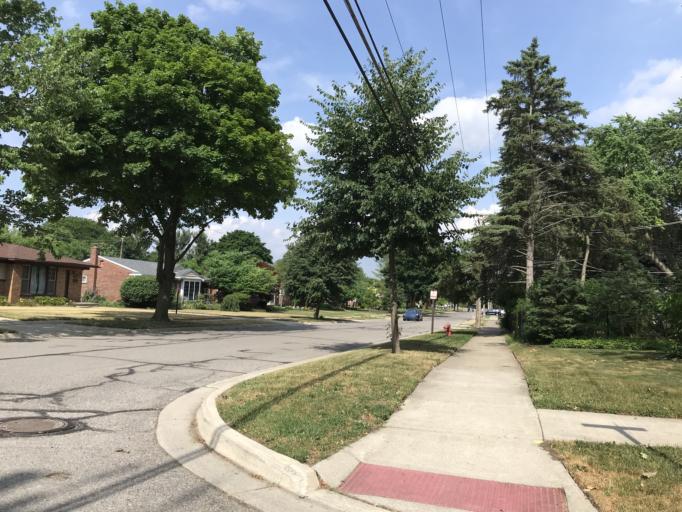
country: US
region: Michigan
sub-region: Oakland County
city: Farmington
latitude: 42.4611
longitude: -83.3737
